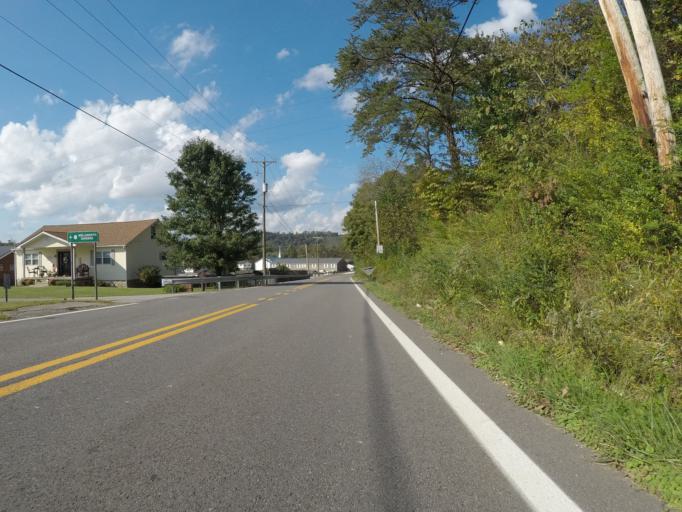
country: US
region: Ohio
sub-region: Lawrence County
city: Burlington
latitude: 38.3623
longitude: -82.5152
